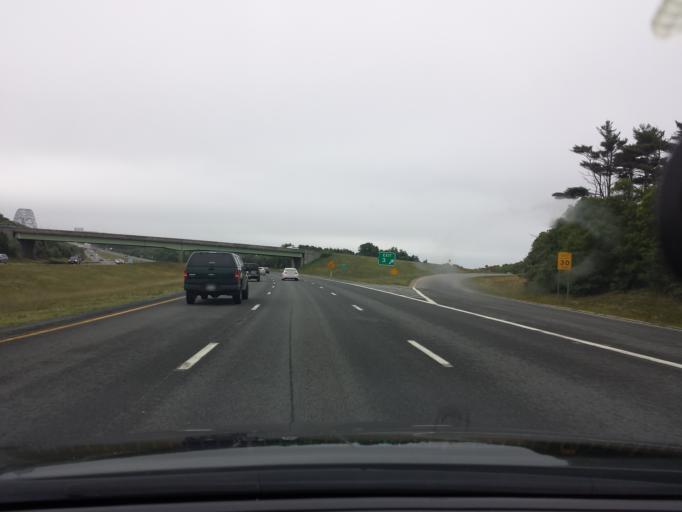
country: US
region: Massachusetts
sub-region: Barnstable County
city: Bourne
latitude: 41.7583
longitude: -70.5946
